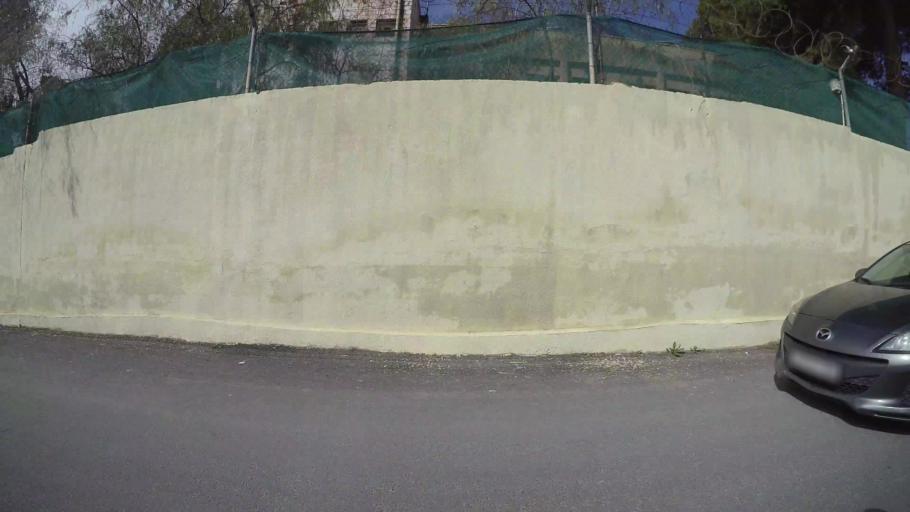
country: JO
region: Amman
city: Al Jubayhah
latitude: 32.0061
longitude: 35.8442
